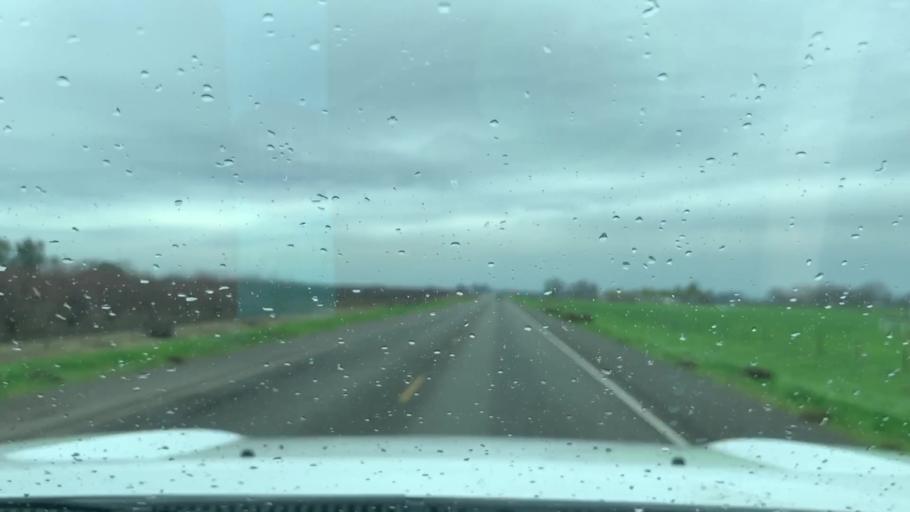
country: US
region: California
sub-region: Fresno County
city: Riverdale
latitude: 36.4129
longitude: -119.8049
